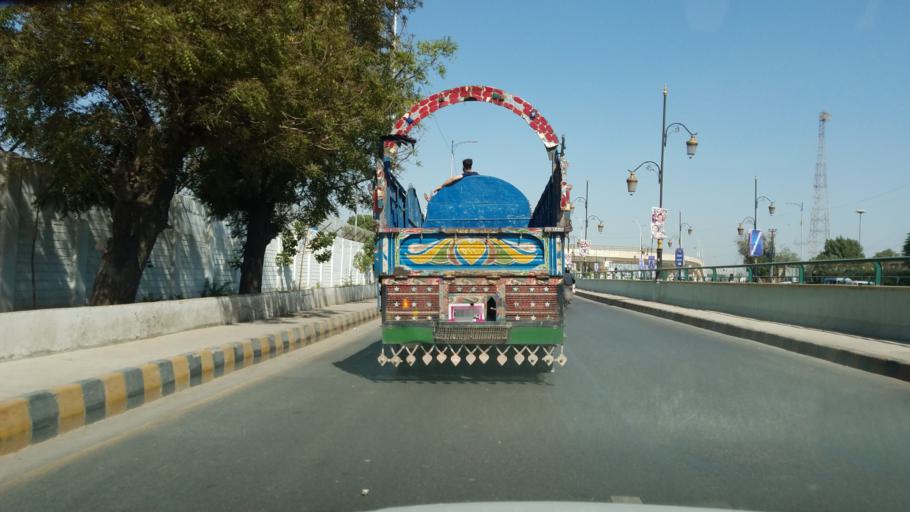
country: PK
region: Sindh
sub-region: Karachi District
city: Karachi
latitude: 24.8869
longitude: 67.1229
